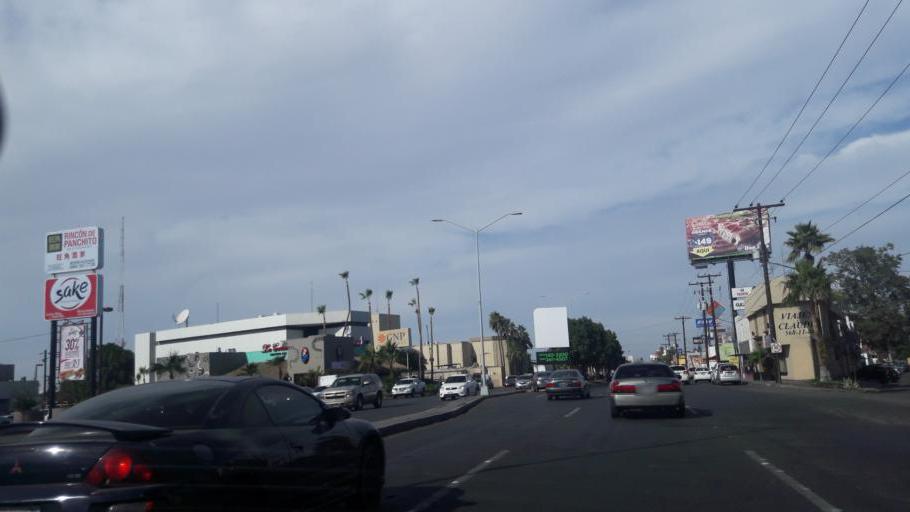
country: MX
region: Baja California
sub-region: Mexicali
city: Mexicali
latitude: 32.6415
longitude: -115.4501
